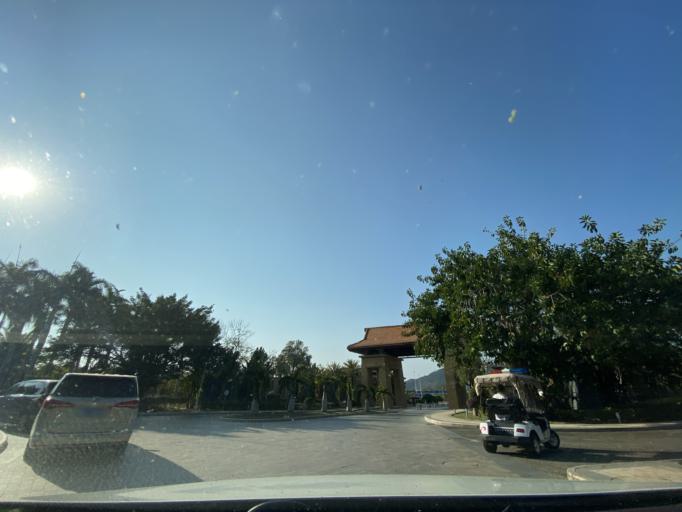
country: CN
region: Hainan
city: Haitangwan
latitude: 18.4033
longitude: 109.7800
